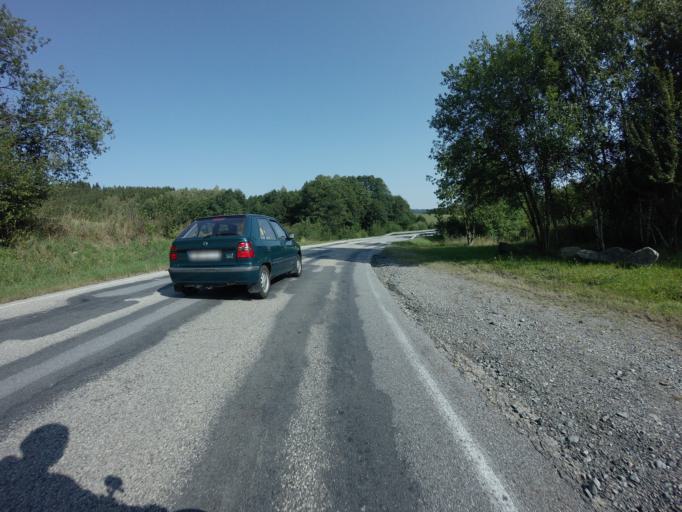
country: CZ
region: Jihocesky
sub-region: Okres Cesky Krumlov
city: Vyssi Brod
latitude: 48.5986
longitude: 14.3208
